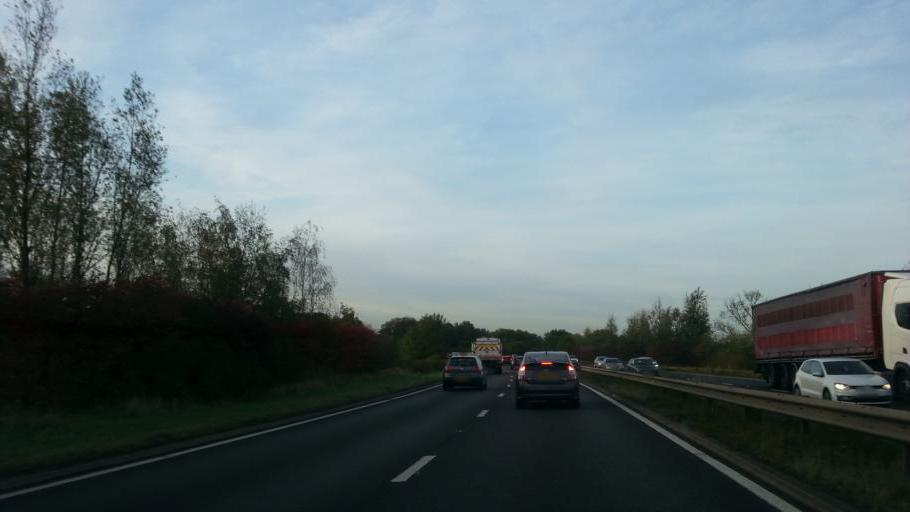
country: GB
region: England
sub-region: Leicestershire
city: Sileby
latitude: 52.7058
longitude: -1.0953
